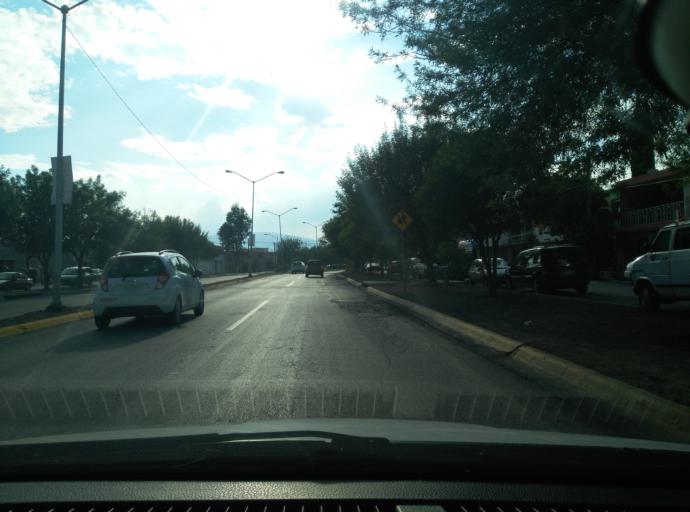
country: MX
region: Nuevo Leon
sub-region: Apodaca
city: Fraccionamiento Cosmopolis Octavo Sector
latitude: 25.7680
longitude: -100.2451
